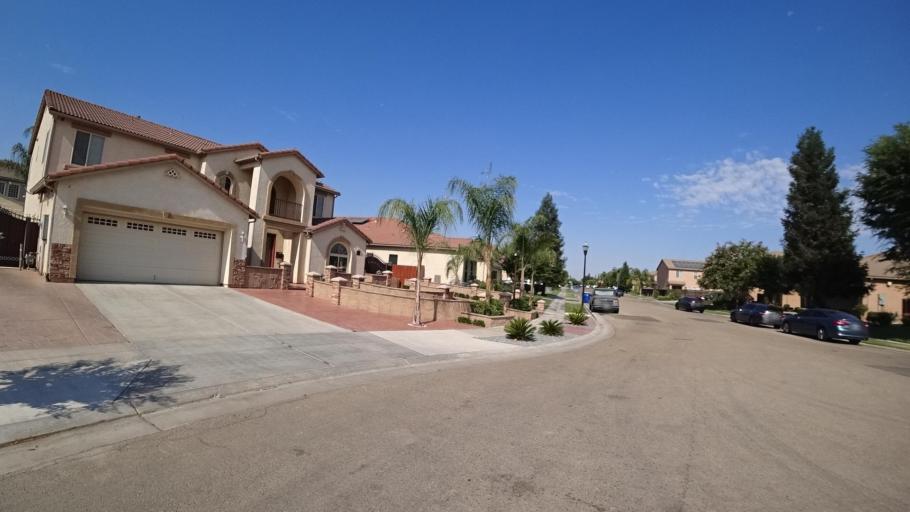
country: US
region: California
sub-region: Fresno County
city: Sunnyside
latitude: 36.7110
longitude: -119.6846
